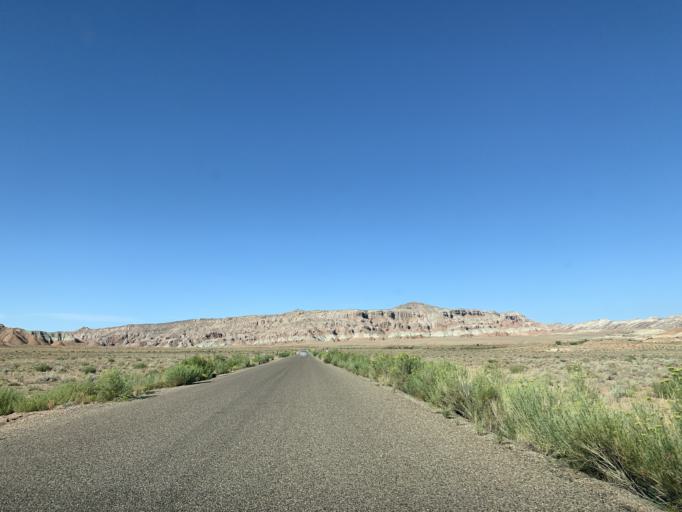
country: US
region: Utah
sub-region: Emery County
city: Ferron
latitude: 38.5780
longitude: -110.7351
